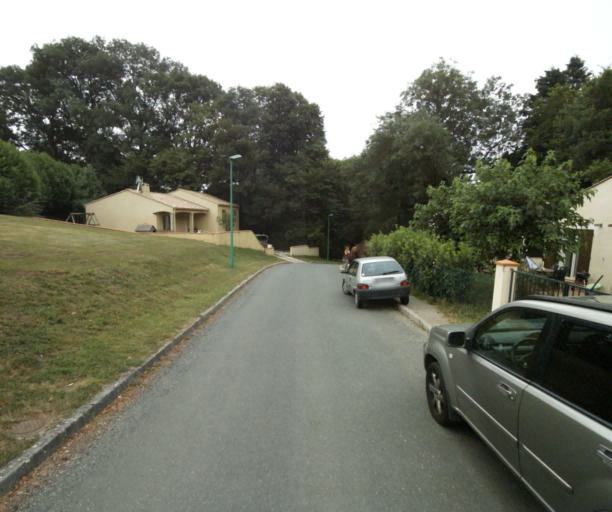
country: FR
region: Midi-Pyrenees
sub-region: Departement du Tarn
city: Soreze
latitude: 43.4091
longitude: 2.0780
